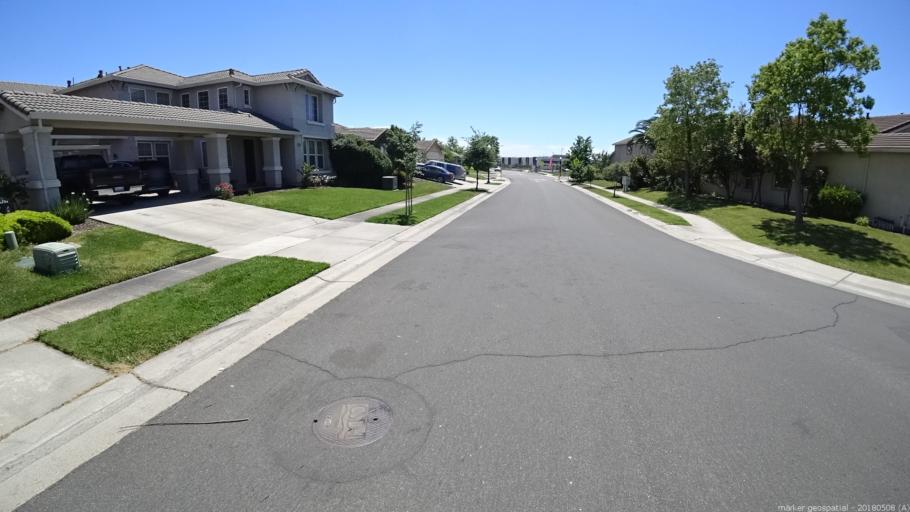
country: US
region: California
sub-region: Sacramento County
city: Elverta
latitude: 38.6773
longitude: -121.5254
